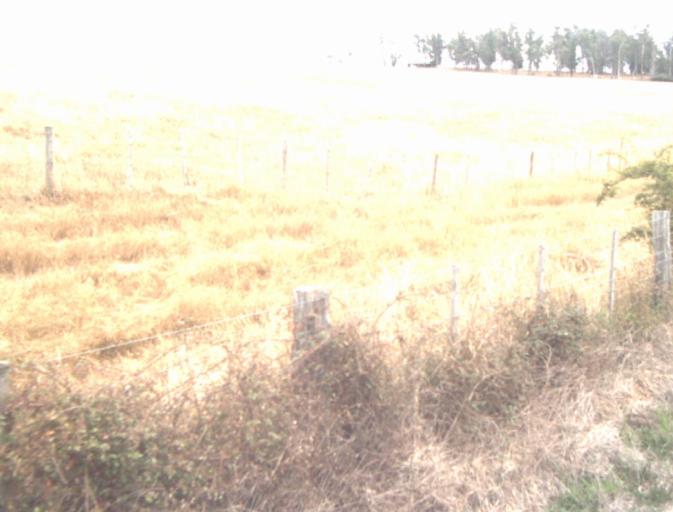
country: AU
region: Tasmania
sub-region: Launceston
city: Mayfield
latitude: -41.2931
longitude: 147.0226
